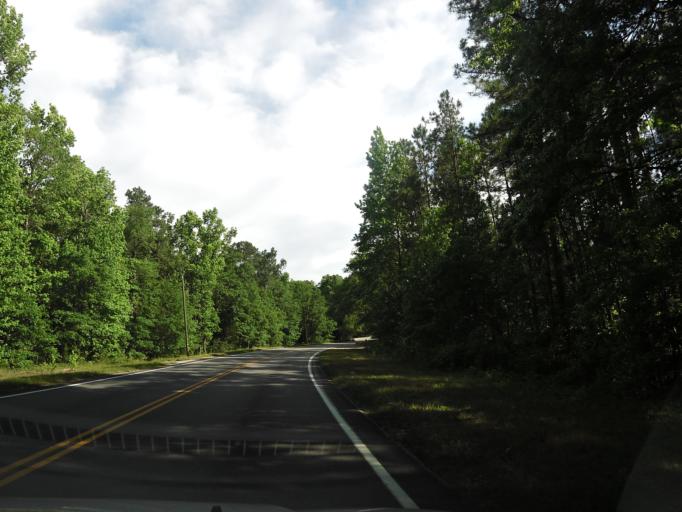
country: US
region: South Carolina
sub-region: Allendale County
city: Fairfax
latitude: 33.0159
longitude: -81.2152
